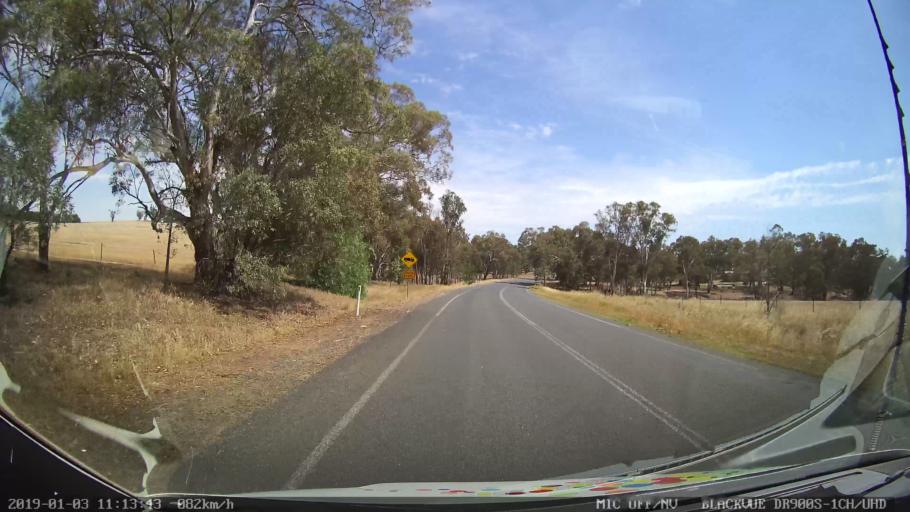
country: AU
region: New South Wales
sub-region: Young
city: Young
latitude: -34.1852
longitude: 148.2604
